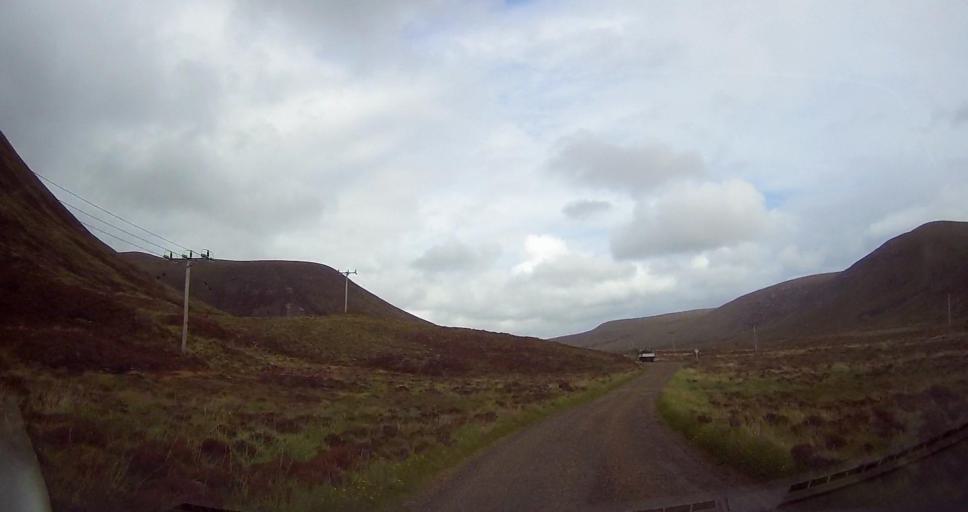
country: GB
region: Scotland
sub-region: Orkney Islands
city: Stromness
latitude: 58.8836
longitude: -3.3380
